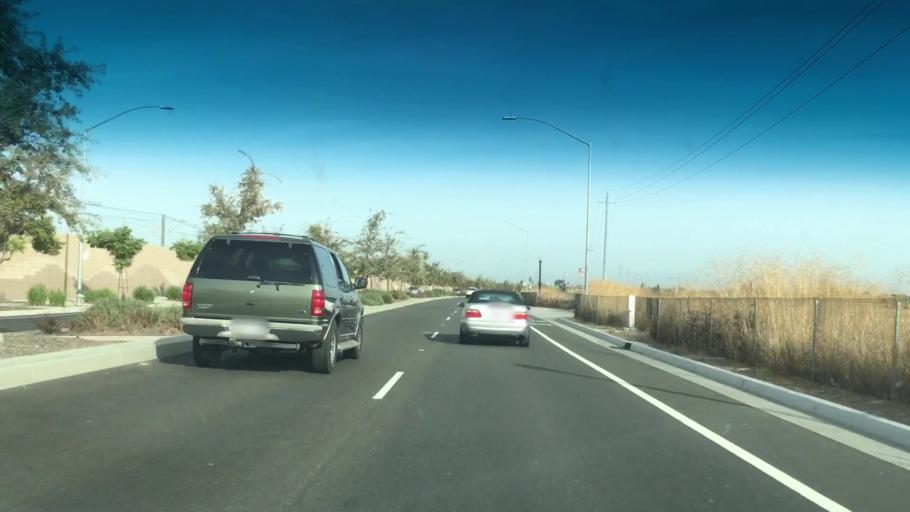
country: US
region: California
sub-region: Sacramento County
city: Parkway
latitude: 38.4615
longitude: -121.4552
